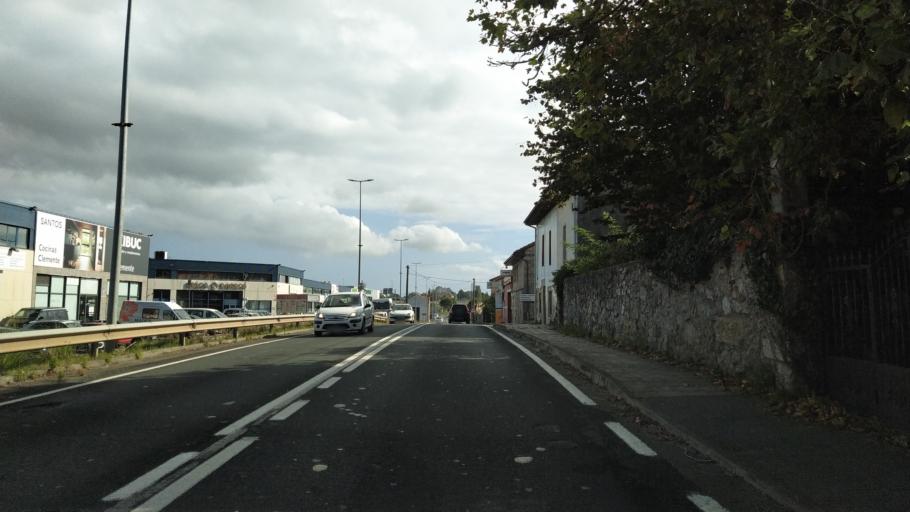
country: ES
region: Cantabria
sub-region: Provincia de Cantabria
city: Santa Cruz de Bezana
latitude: 43.4382
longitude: -3.8945
